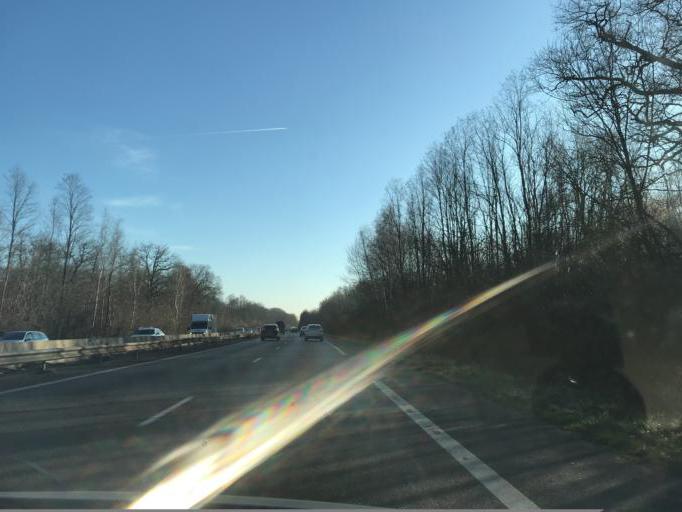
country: FR
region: Ile-de-France
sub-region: Departement de Seine-et-Marne
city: Lesigny
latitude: 48.7603
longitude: 2.6157
